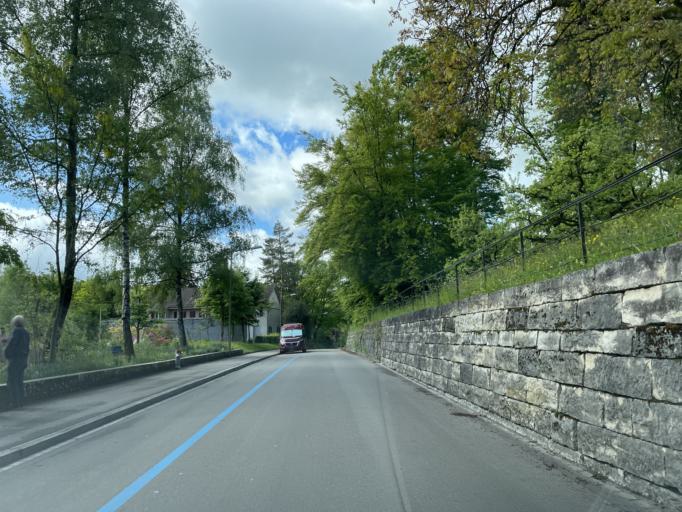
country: CH
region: Zurich
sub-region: Bezirk Winterthur
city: Stadt Winterthur (Kreis 1) / Heiligberg
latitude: 47.4941
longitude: 8.7263
